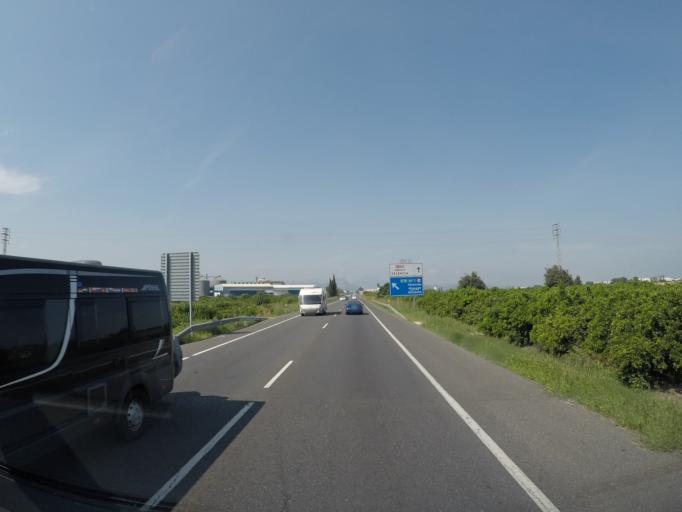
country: ES
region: Valencia
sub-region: Provincia de Valencia
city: Oliva
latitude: 38.9262
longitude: -0.1284
